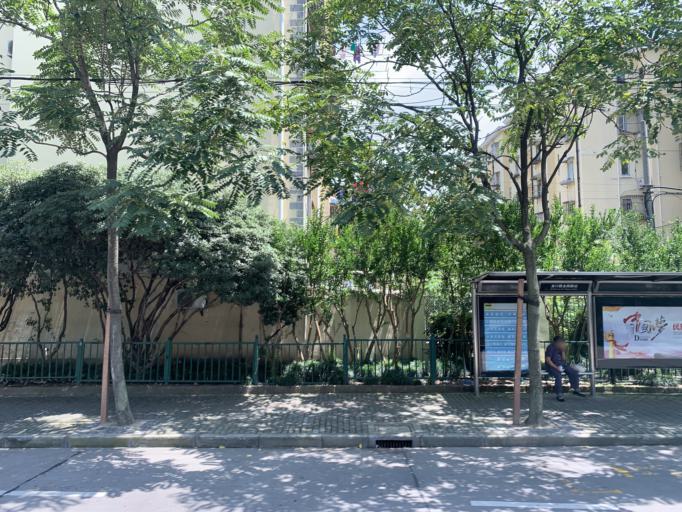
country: CN
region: Shanghai Shi
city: Pudong
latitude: 31.2495
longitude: 121.5750
